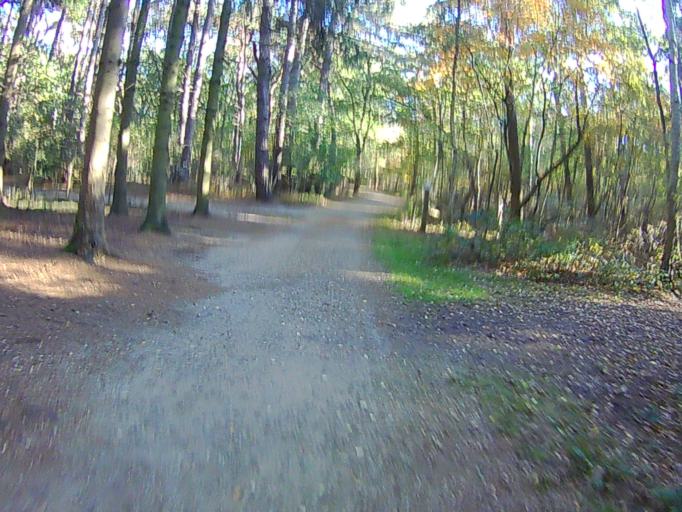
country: BE
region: Flanders
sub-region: Provincie Antwerpen
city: Stabroek
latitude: 51.3386
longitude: 4.3917
